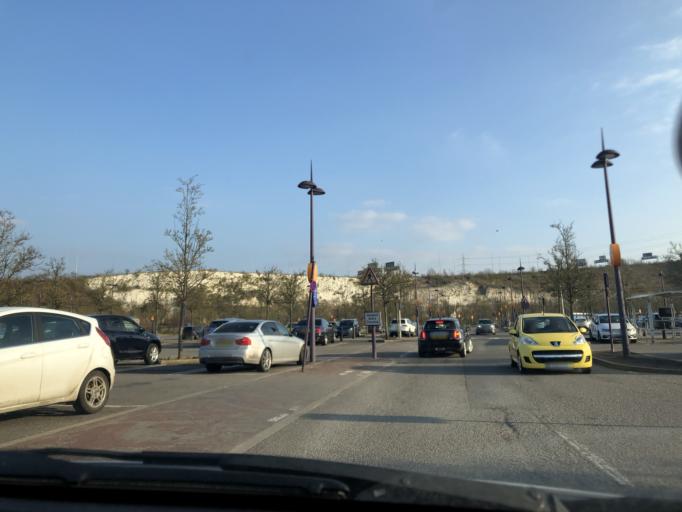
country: GB
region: England
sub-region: Kent
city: Greenhithe
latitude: 51.4395
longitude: 0.2754
